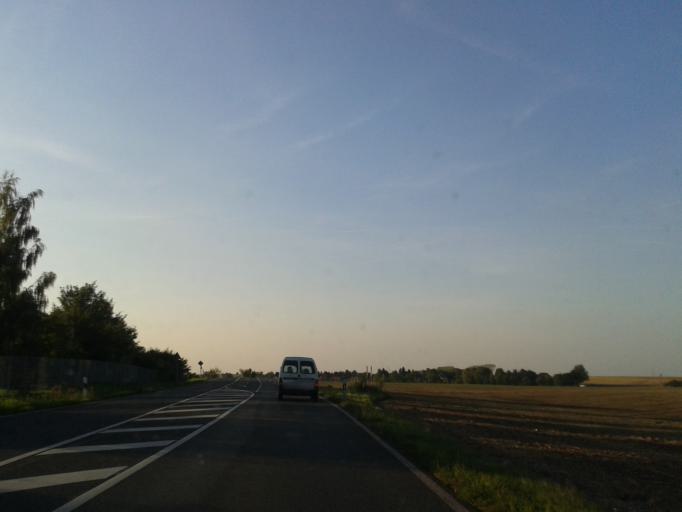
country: DE
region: Saxony
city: Klipphausen
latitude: 51.0706
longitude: 13.5138
